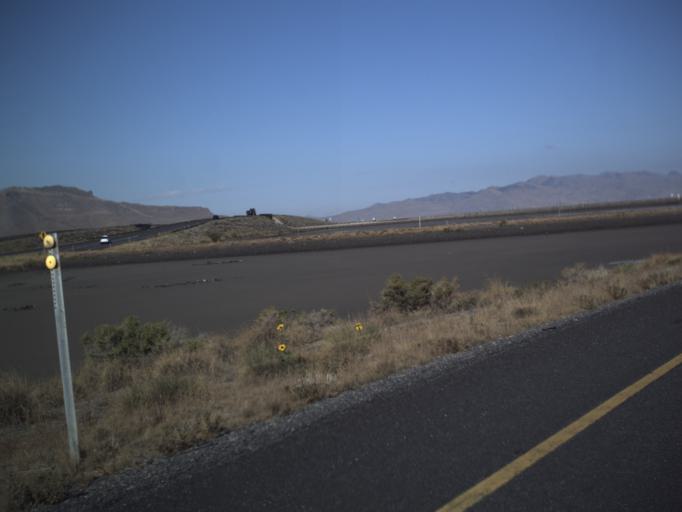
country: US
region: Utah
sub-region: Tooele County
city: Grantsville
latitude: 40.7074
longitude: -112.5215
